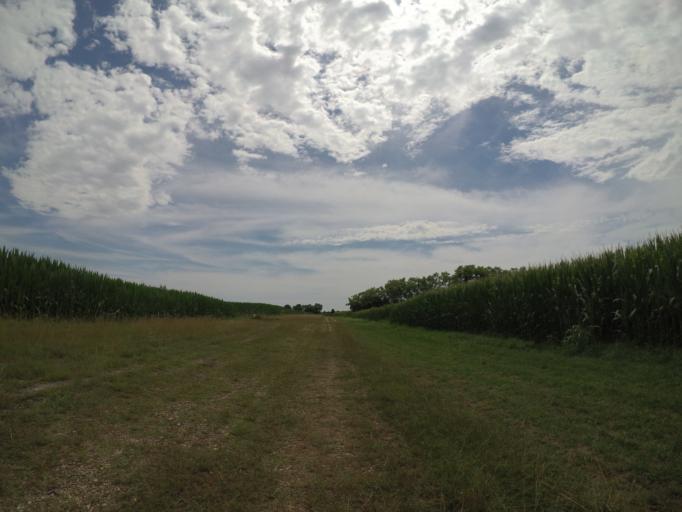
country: IT
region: Friuli Venezia Giulia
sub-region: Provincia di Udine
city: Bertiolo
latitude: 45.9719
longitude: 13.0588
